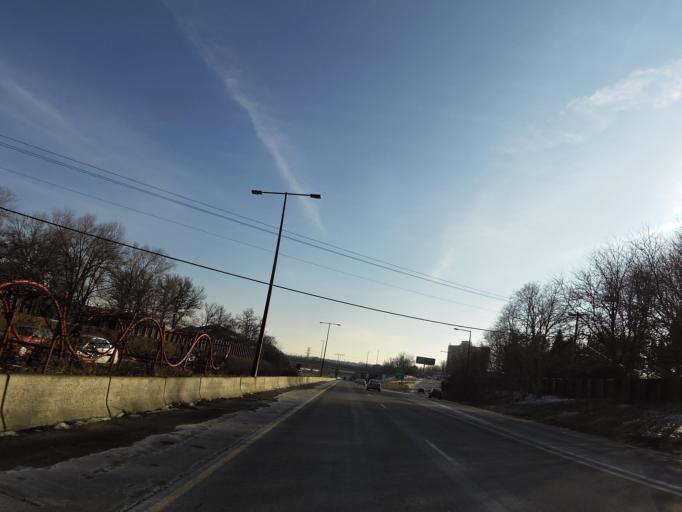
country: US
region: Minnesota
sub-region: Dakota County
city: Mendota Heights
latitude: 44.9182
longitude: -93.1447
